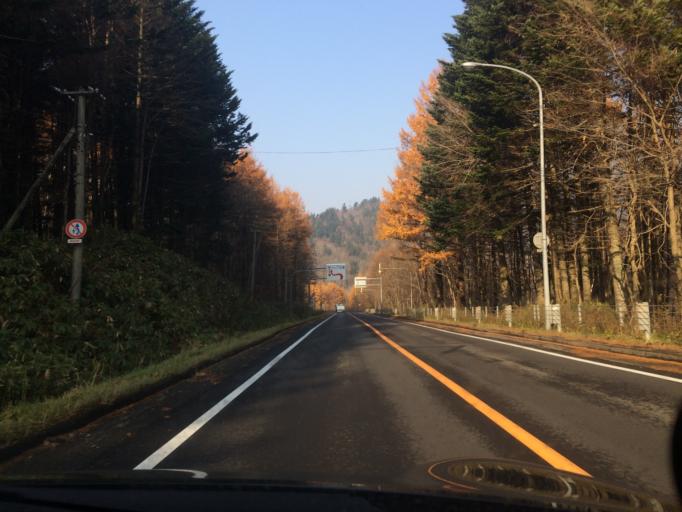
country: JP
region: Hokkaido
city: Iwamizawa
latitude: 42.9291
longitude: 142.1135
